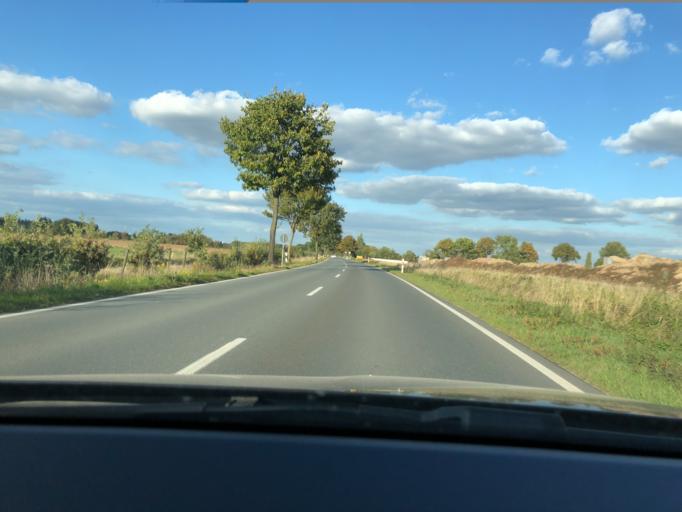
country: DE
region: Lower Saxony
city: Stuhr
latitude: 53.0222
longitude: 8.7831
